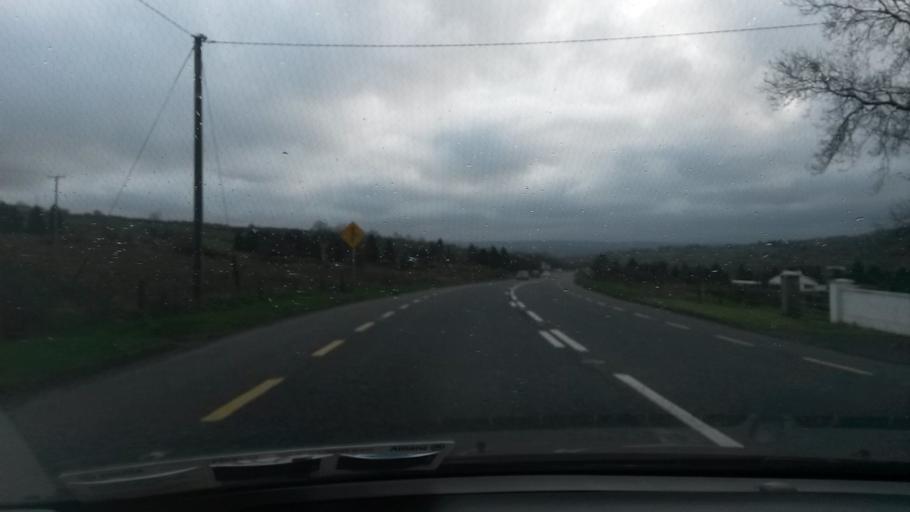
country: IE
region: Munster
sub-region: County Limerick
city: Newcastle West
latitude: 52.4111
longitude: -9.1557
